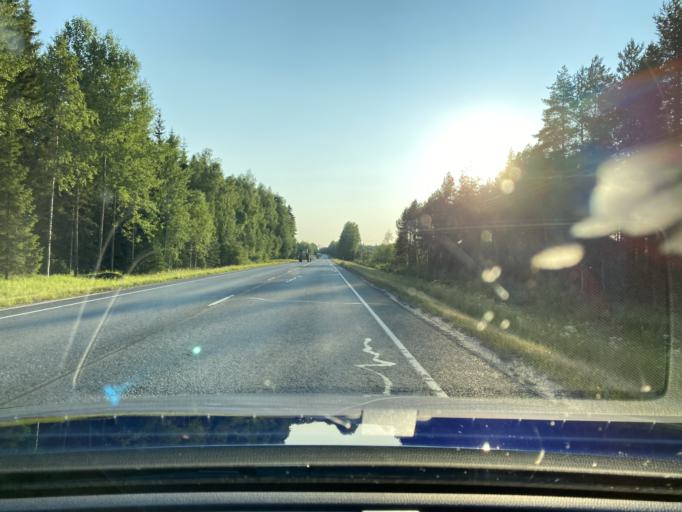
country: FI
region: Haeme
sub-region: Forssa
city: Tammela
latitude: 60.8273
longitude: 23.8988
